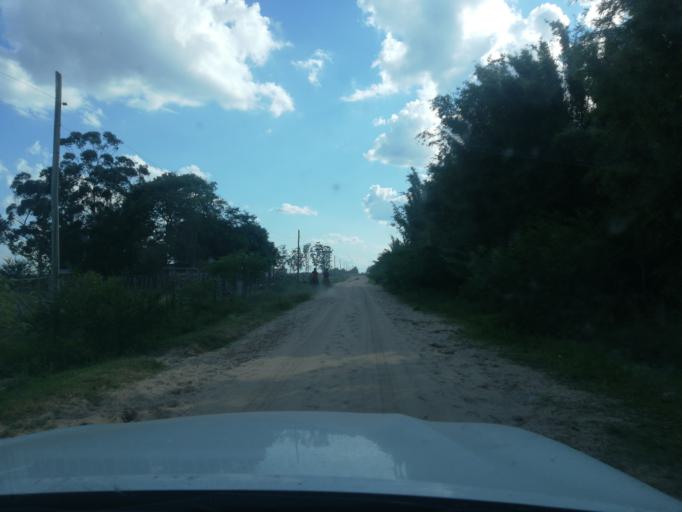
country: AR
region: Corrientes
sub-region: Departamento de San Miguel
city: San Miguel
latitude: -27.9945
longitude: -57.5776
